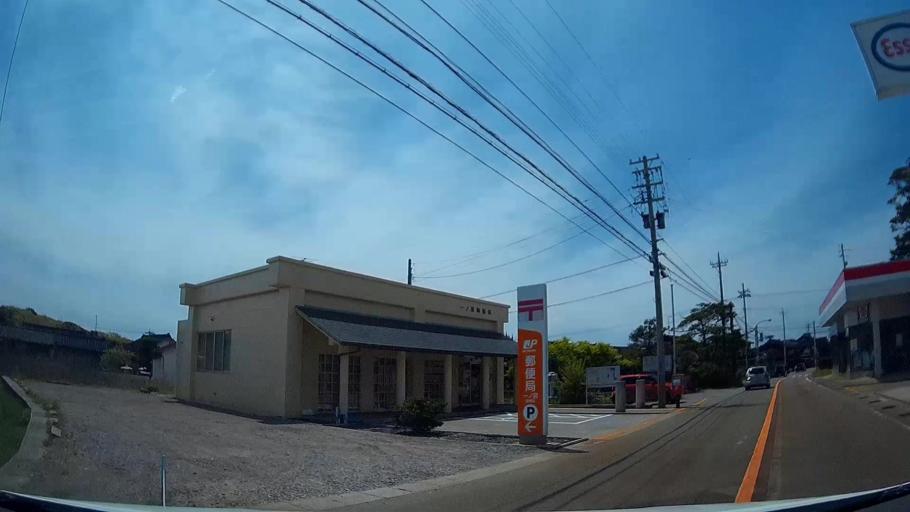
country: JP
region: Ishikawa
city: Hakui
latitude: 36.9234
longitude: 136.7677
